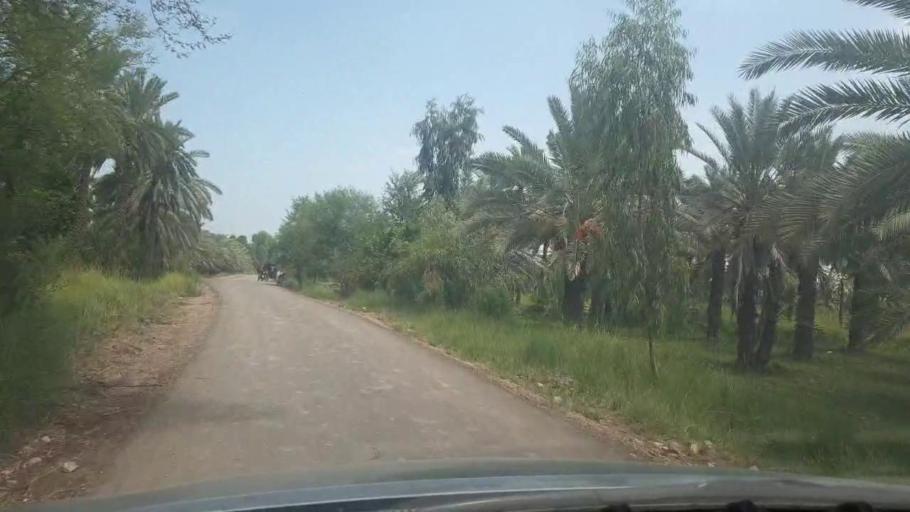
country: PK
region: Sindh
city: Kot Diji
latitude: 27.3922
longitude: 68.7676
